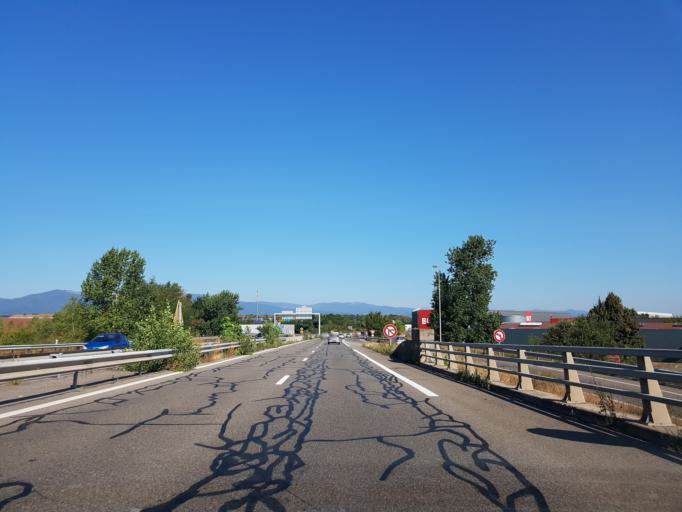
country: FR
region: Alsace
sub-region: Departement du Haut-Rhin
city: Kingersheim
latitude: 47.7909
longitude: 7.3140
